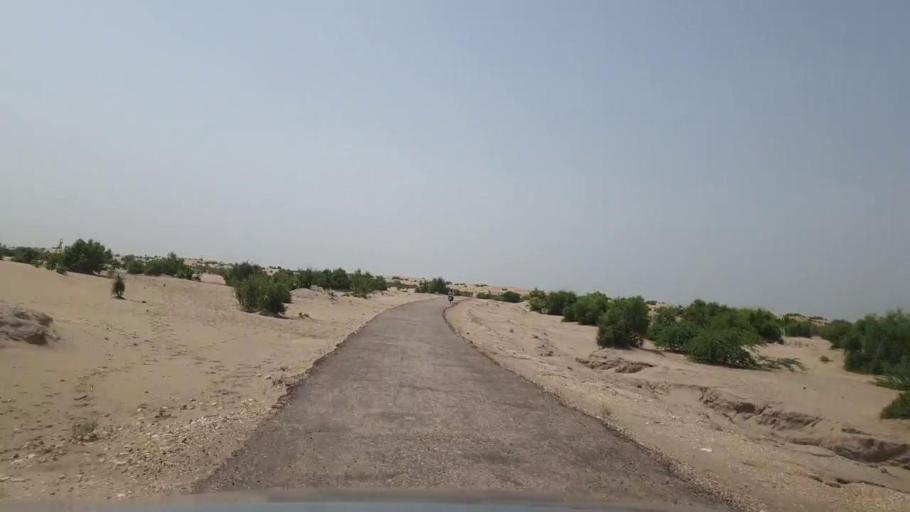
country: PK
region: Sindh
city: Pano Aqil
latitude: 27.6057
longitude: 69.1468
